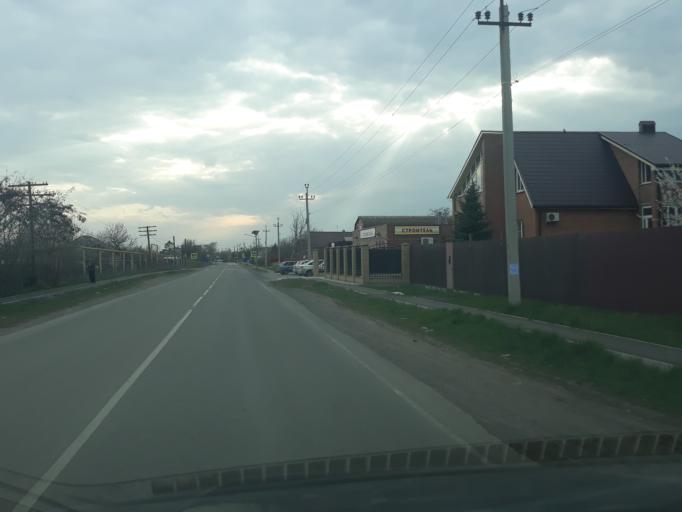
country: RU
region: Rostov
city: Novobessergenovka
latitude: 47.1752
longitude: 38.7677
